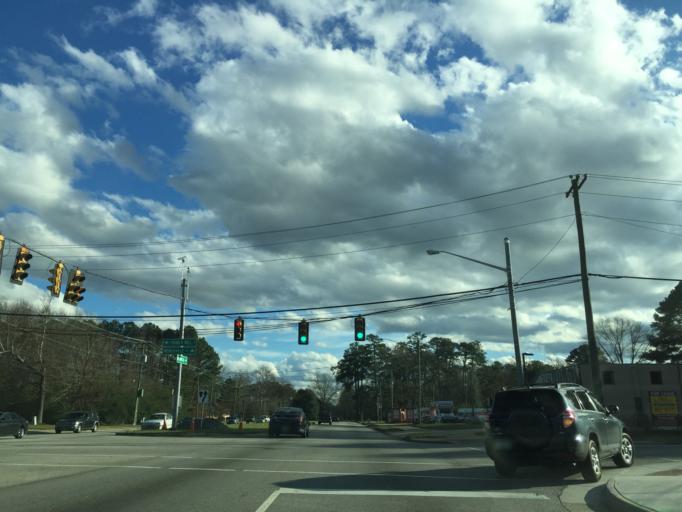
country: US
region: Virginia
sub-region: York County
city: Yorktown
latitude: 37.1108
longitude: -76.5171
